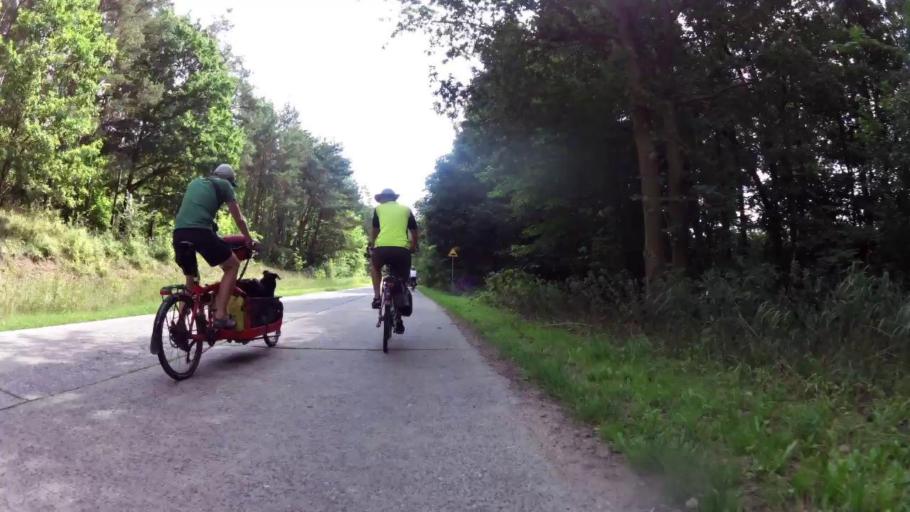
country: PL
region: West Pomeranian Voivodeship
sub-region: Powiat drawski
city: Drawsko Pomorskie
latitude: 53.4732
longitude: 15.7806
